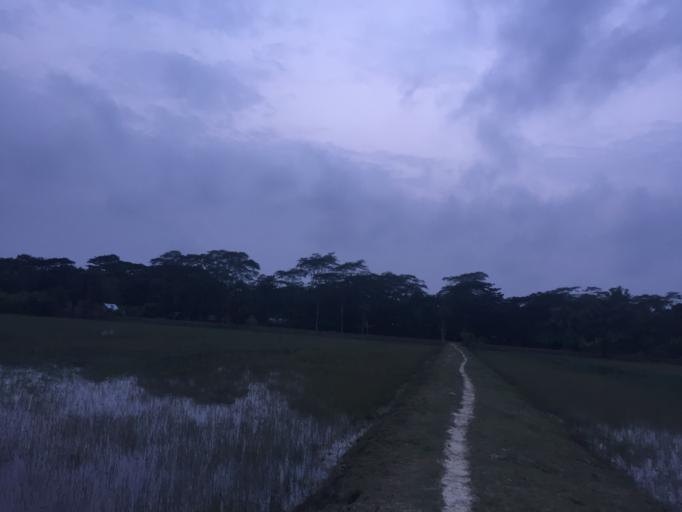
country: BD
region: Barisal
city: Mathba
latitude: 22.1935
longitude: 89.9335
